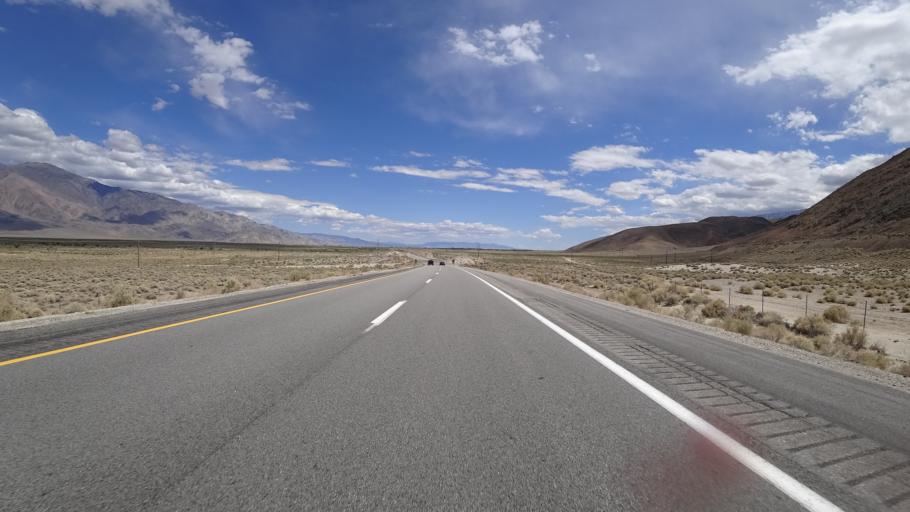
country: US
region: California
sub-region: Inyo County
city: Lone Pine
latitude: 36.6514
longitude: -118.0926
